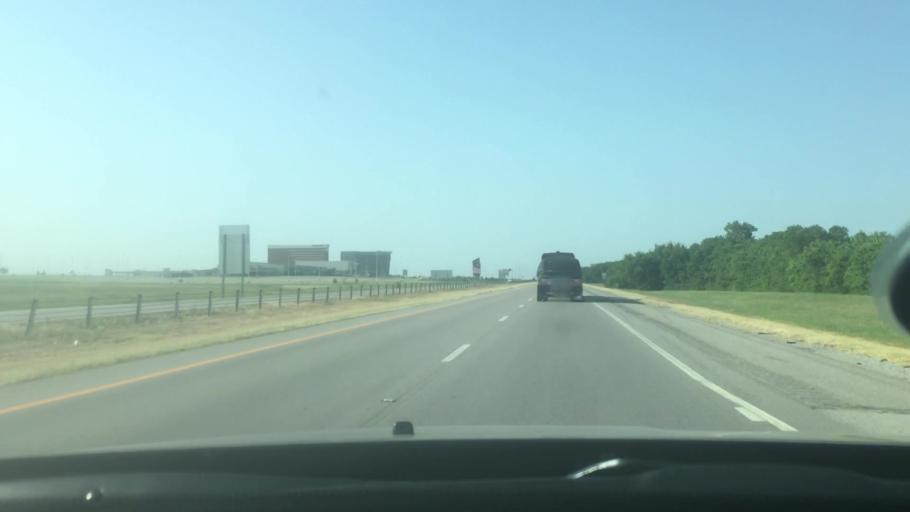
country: US
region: Oklahoma
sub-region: Bryan County
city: Calera
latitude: 33.9633
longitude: -96.4168
